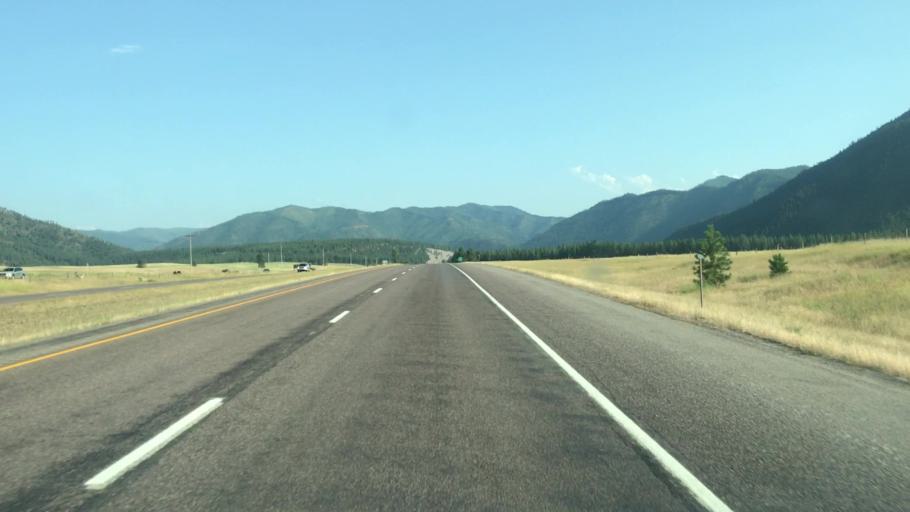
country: US
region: Montana
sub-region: Mineral County
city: Superior
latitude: 47.0474
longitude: -114.7537
